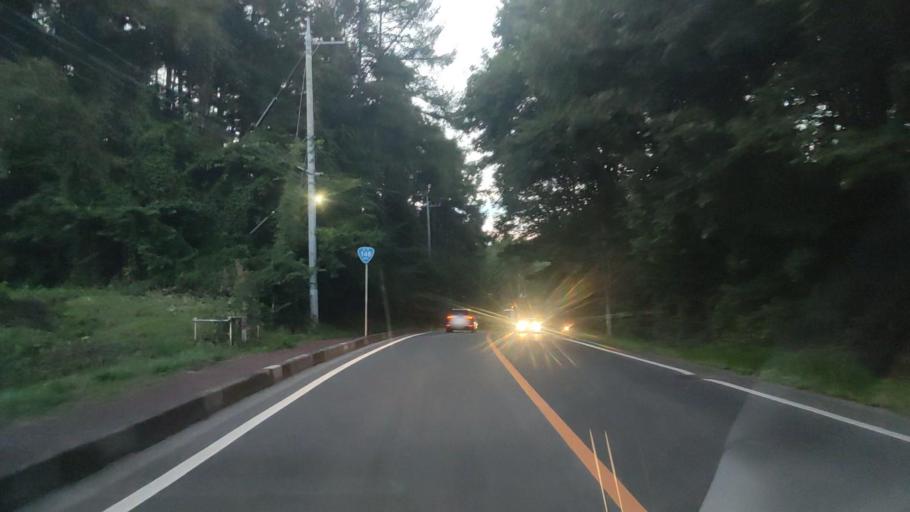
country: JP
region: Gunma
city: Nakanojomachi
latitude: 36.5185
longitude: 138.5982
